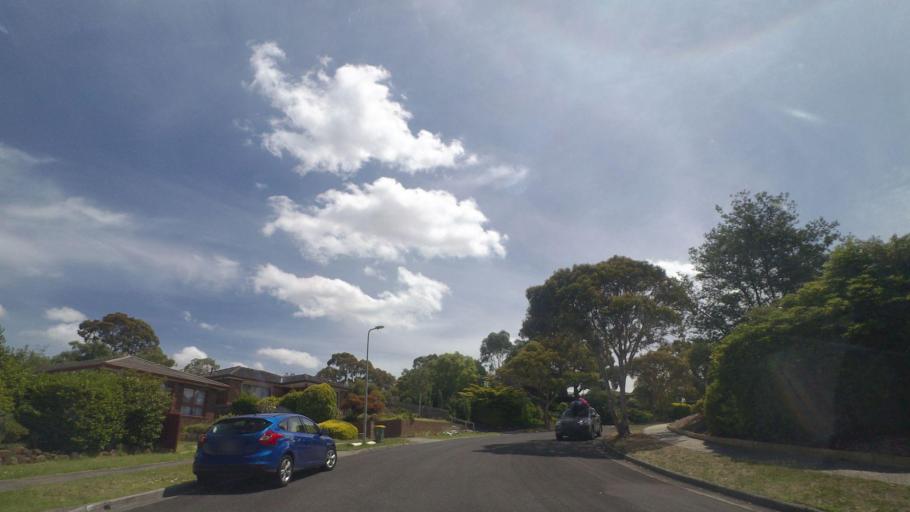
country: AU
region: Victoria
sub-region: Maroondah
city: Bayswater North
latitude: -37.8431
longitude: 145.2962
